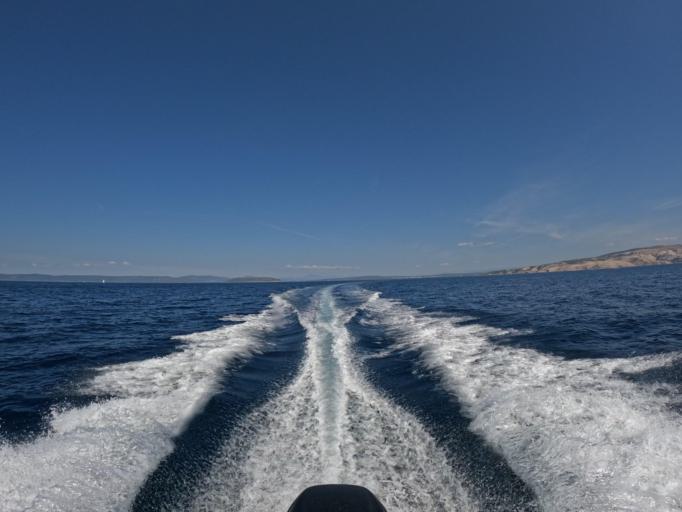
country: HR
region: Primorsko-Goranska
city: Punat
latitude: 44.9073
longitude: 14.6303
